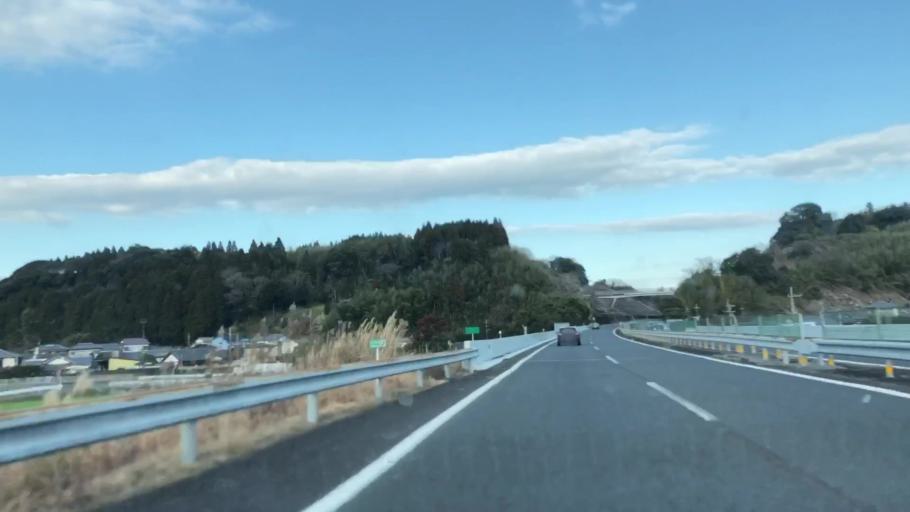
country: JP
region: Miyazaki
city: Miyazaki-shi
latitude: 31.8625
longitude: 131.3812
